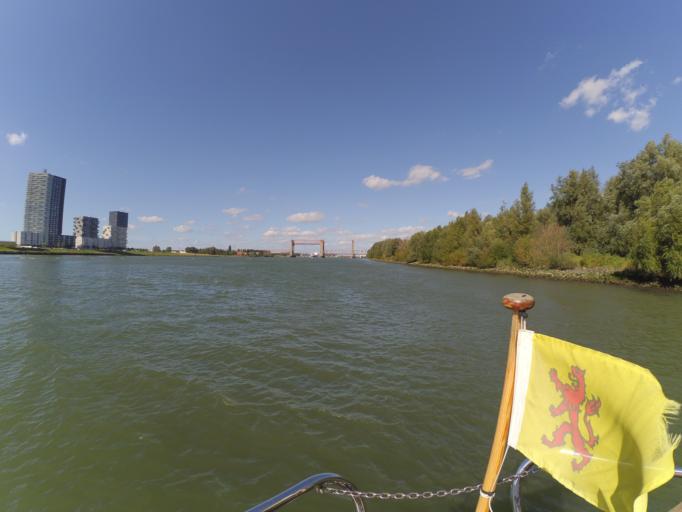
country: NL
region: South Holland
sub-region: Gemeente Spijkenisse
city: Spijkenisse
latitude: 51.8530
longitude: 4.3497
